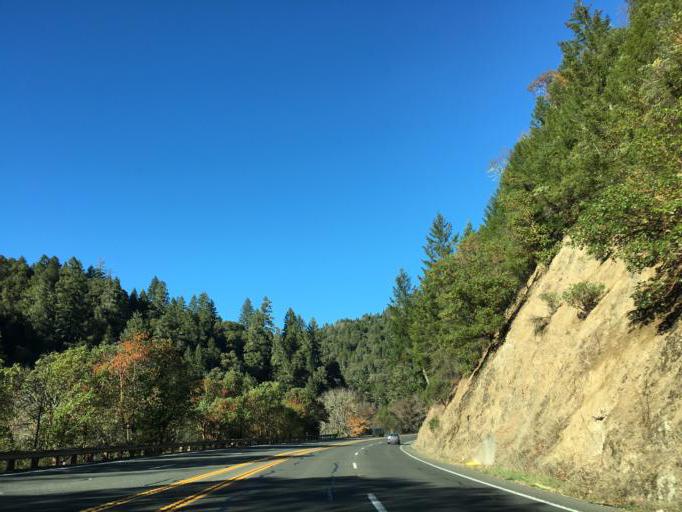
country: US
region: California
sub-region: Mendocino County
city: Brooktrails
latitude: 39.5310
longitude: -123.4045
